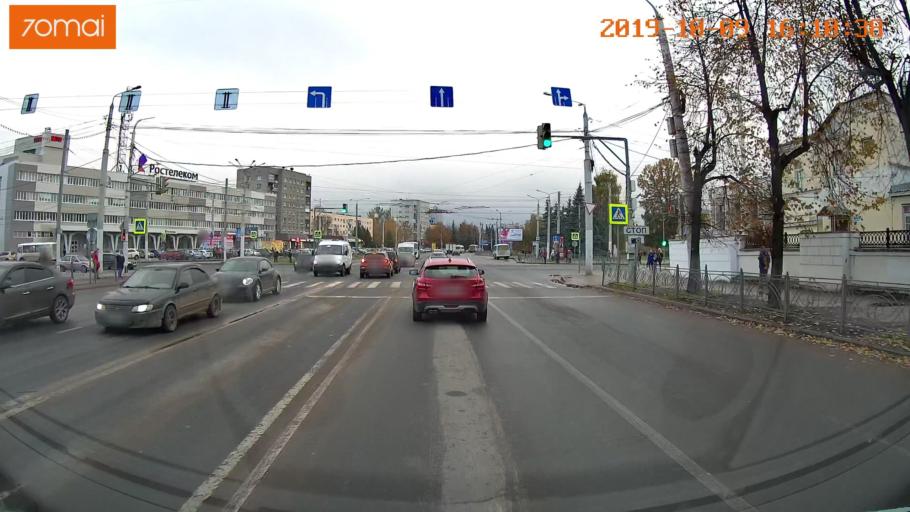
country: RU
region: Kostroma
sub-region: Kostromskoy Rayon
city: Kostroma
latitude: 57.7617
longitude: 40.9514
